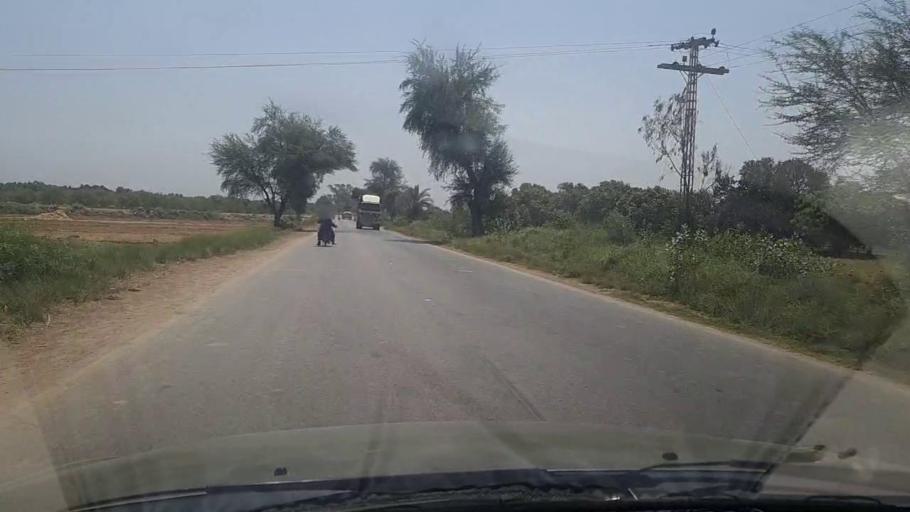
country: PK
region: Sindh
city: Tando Jam
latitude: 25.3548
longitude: 68.5025
